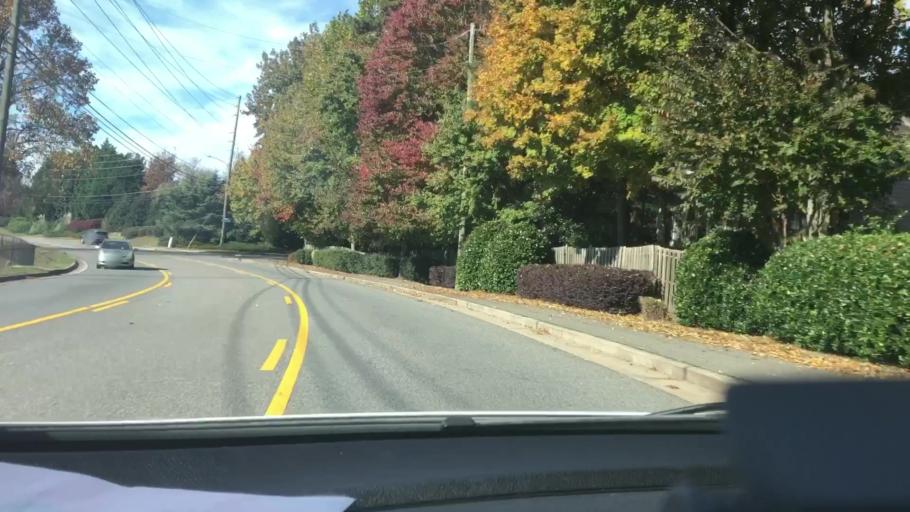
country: US
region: Georgia
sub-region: Gwinnett County
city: Berkeley Lake
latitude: 33.9702
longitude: -84.1995
